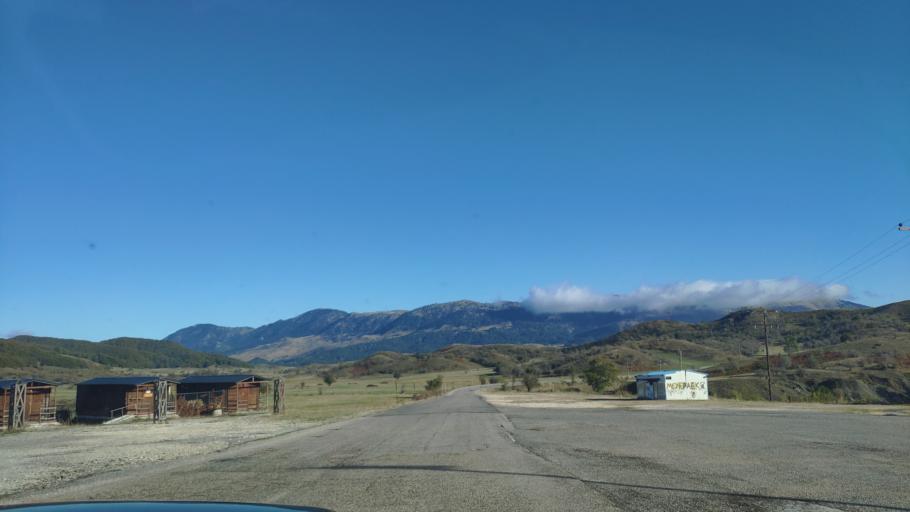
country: GR
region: Epirus
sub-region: Nomos Ioanninon
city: Metsovo
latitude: 39.7848
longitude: 21.1589
